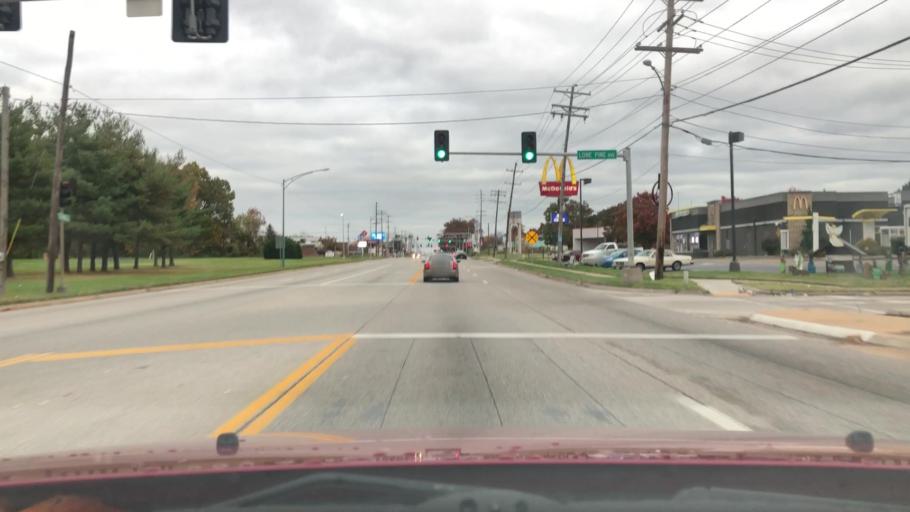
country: US
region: Missouri
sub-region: Greene County
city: Springfield
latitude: 37.1809
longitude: -93.2474
